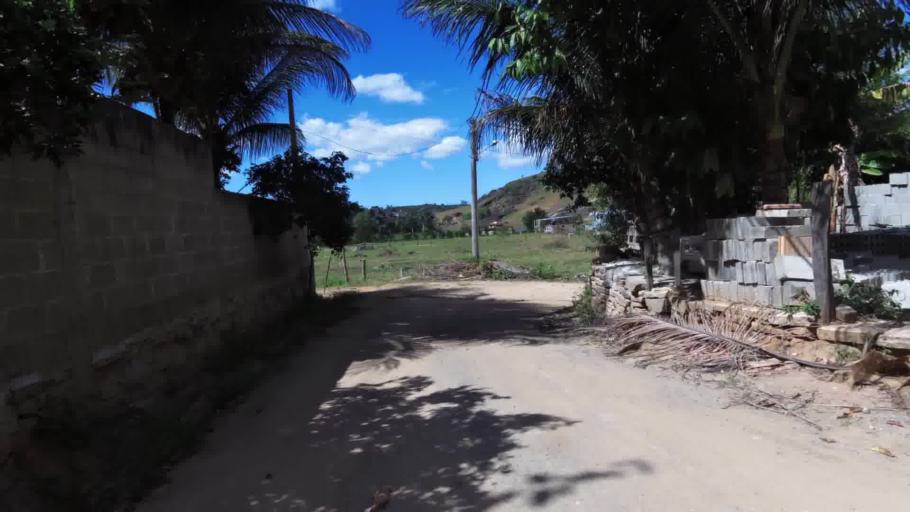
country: BR
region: Espirito Santo
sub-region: Rio Novo Do Sul
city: Rio Novo do Sul
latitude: -20.8605
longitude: -40.9486
